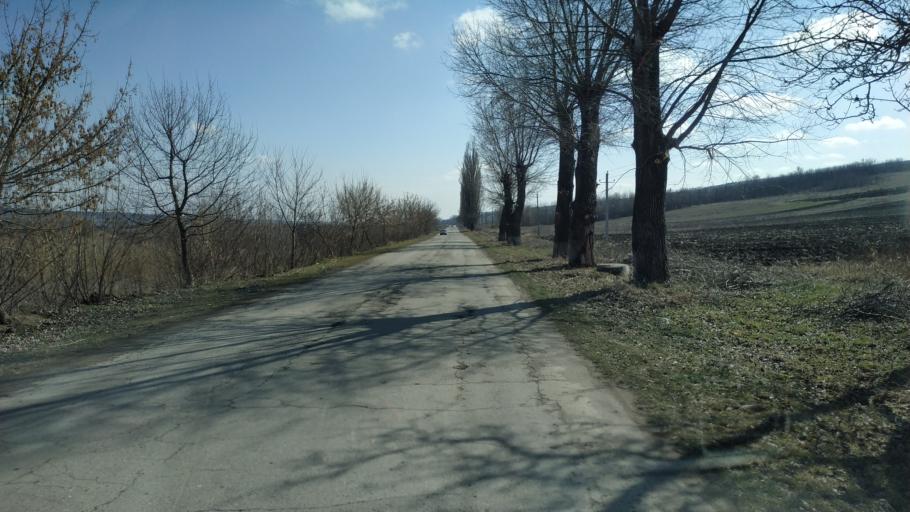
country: MD
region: Hincesti
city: Hincesti
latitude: 46.9478
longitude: 28.6173
